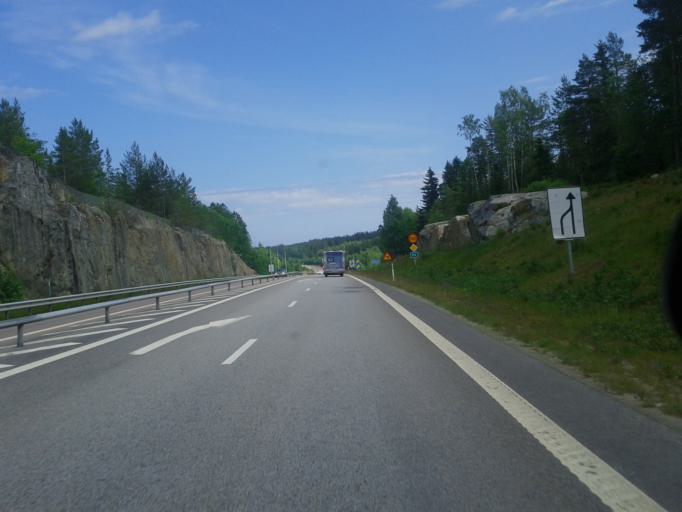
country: SE
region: Vaesternorrland
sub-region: OErnskoeldsviks Kommun
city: Husum
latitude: 63.3512
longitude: 19.1538
